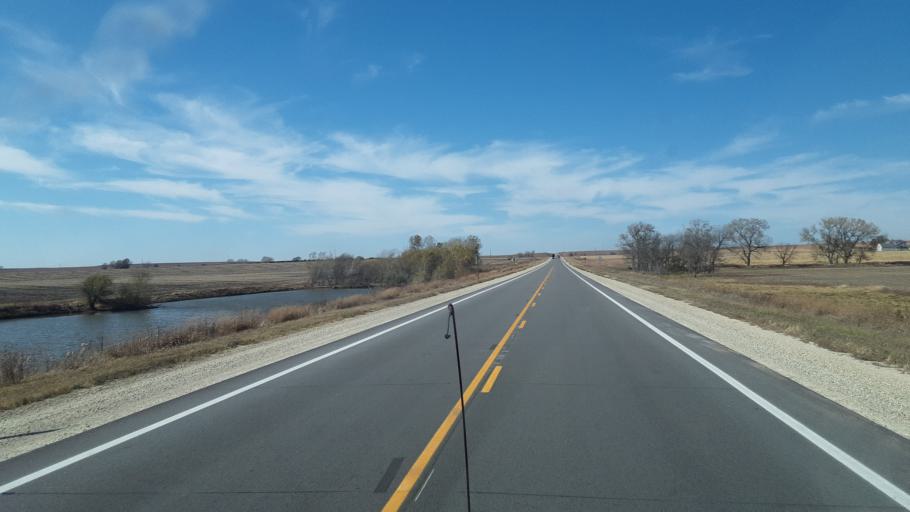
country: US
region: Kansas
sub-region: Chase County
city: Cottonwood Falls
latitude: 38.3627
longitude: -96.6637
